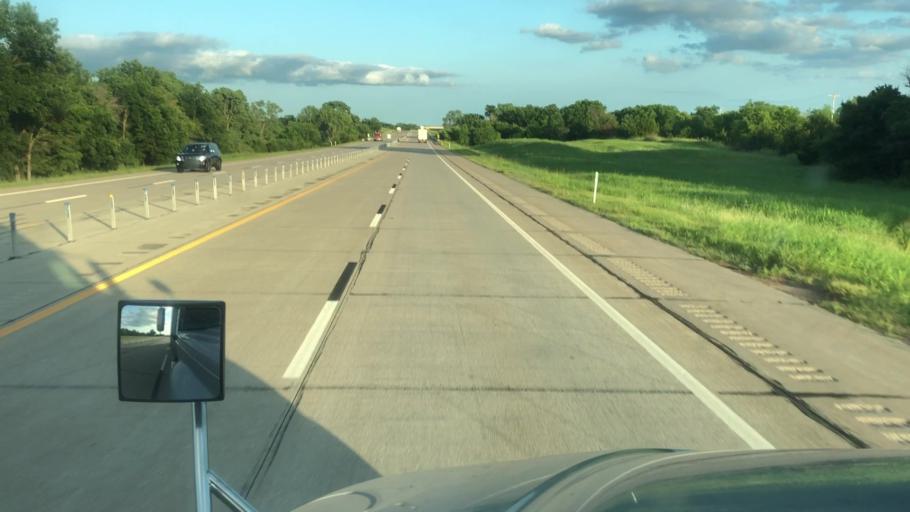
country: US
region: Oklahoma
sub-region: Pawnee County
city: Pawnee
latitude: 36.3265
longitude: -97.0061
